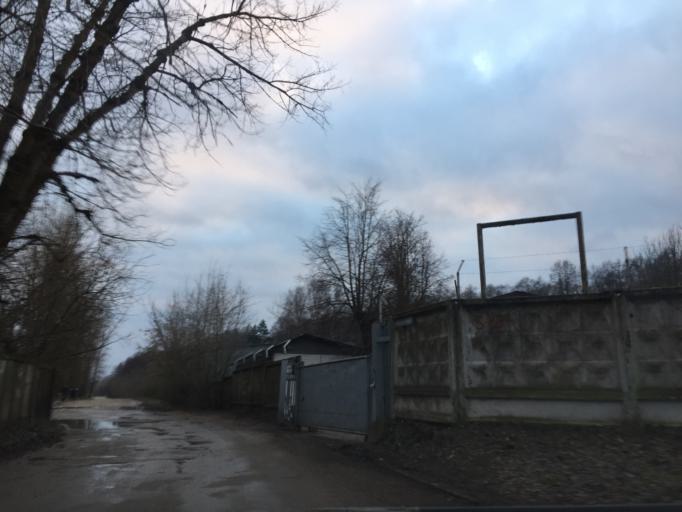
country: LV
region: Kekava
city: Kekava
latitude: 56.8973
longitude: 24.2022
